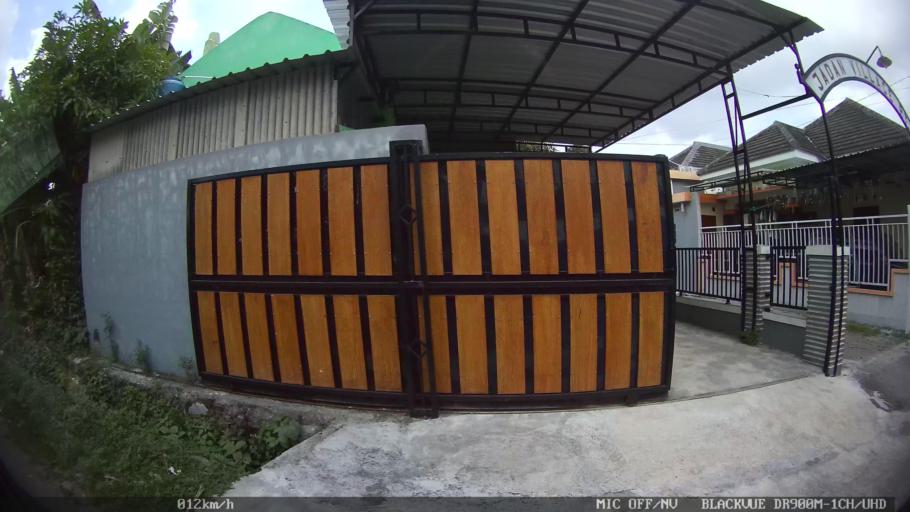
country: ID
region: Daerah Istimewa Yogyakarta
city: Kasihan
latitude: -7.8188
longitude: 110.3265
